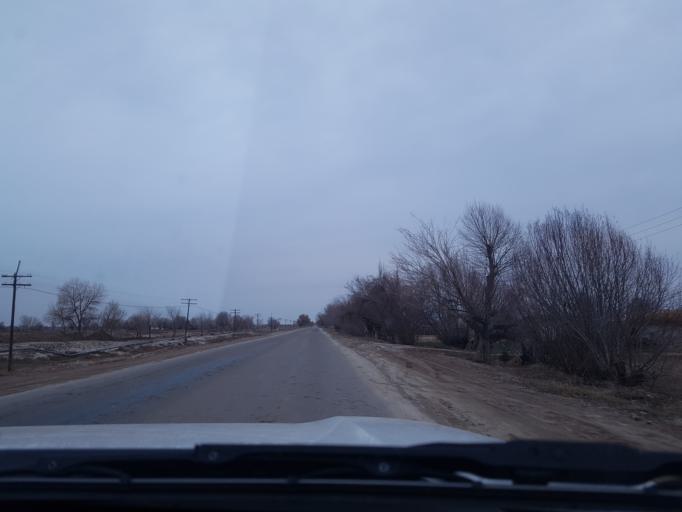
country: TM
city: Akdepe
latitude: 41.9819
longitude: 59.4672
